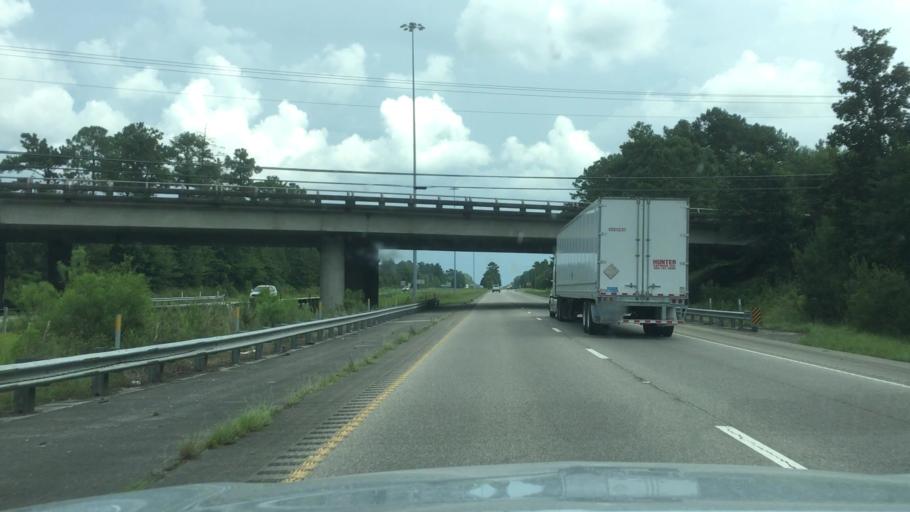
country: US
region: Mississippi
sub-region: Pearl River County
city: Picayune
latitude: 30.5425
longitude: -89.6500
